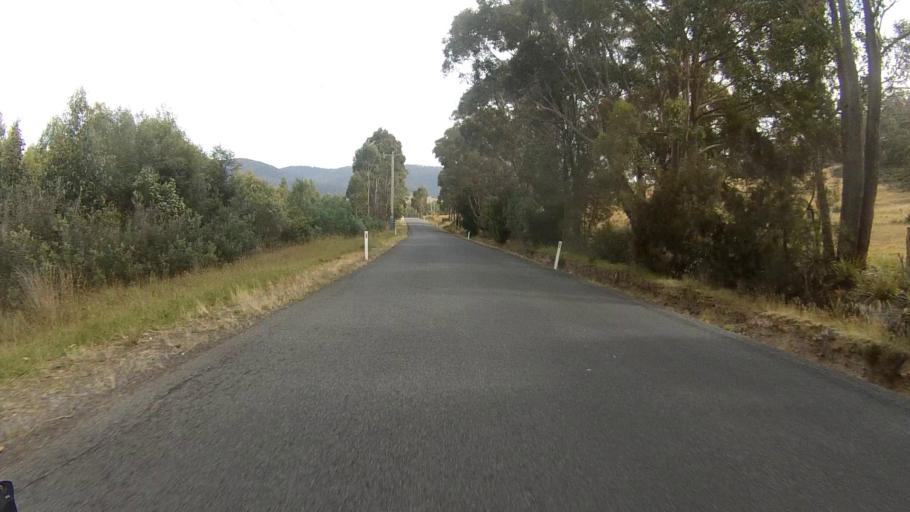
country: AU
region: Tasmania
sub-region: Sorell
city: Sorell
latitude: -42.8075
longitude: 147.7945
